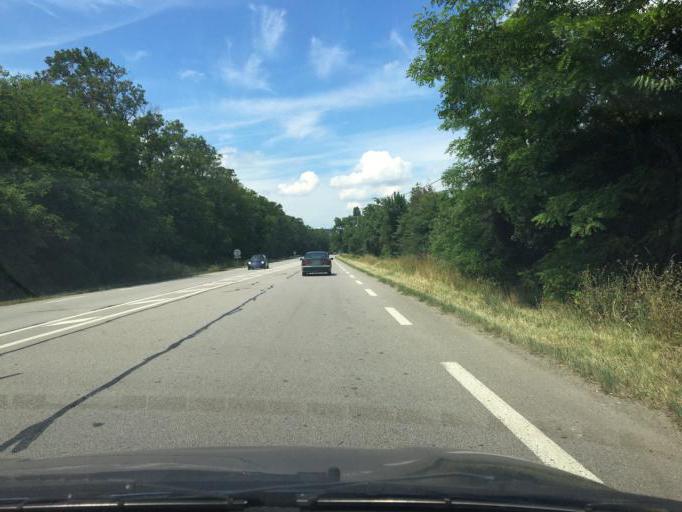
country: FR
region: Rhone-Alpes
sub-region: Departement de l'Ardeche
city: Charmes-sur-Rhone
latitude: 44.8551
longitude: 4.8525
